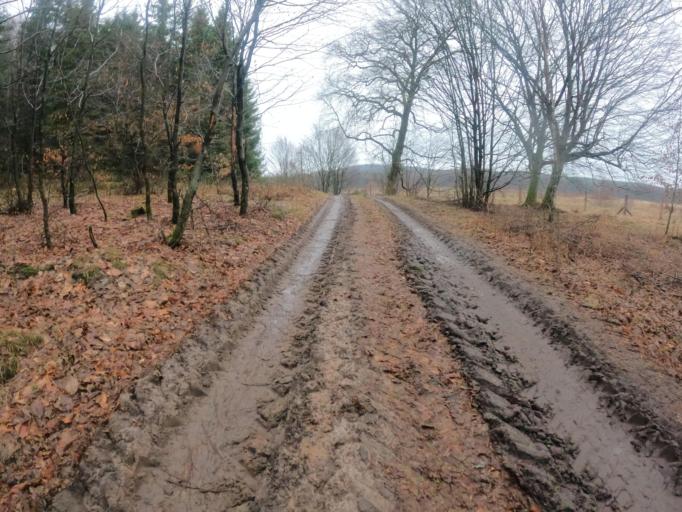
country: PL
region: West Pomeranian Voivodeship
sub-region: Powiat koszalinski
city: Polanow
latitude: 54.2296
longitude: 16.7236
